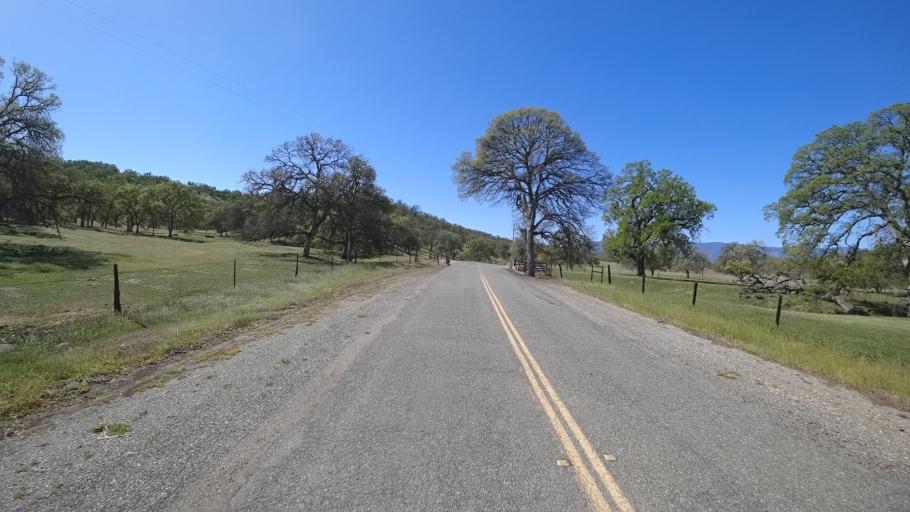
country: US
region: California
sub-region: Tehama County
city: Rancho Tehama Reserve
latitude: 39.7887
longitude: -122.4574
